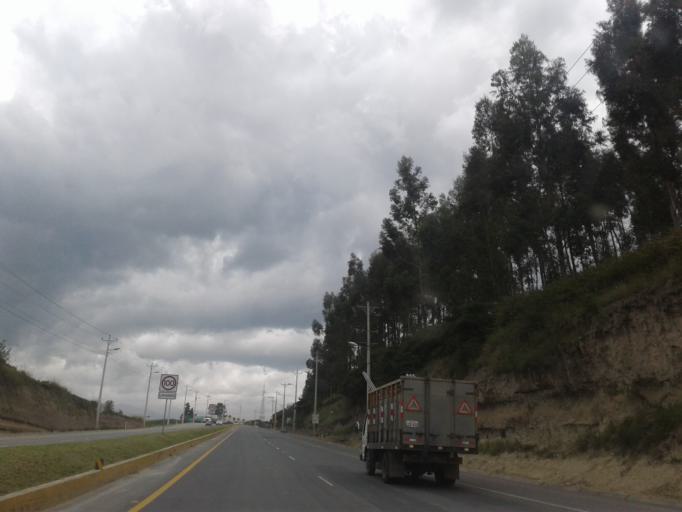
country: EC
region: Pichincha
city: Sangolqui
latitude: -0.3078
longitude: -78.3643
